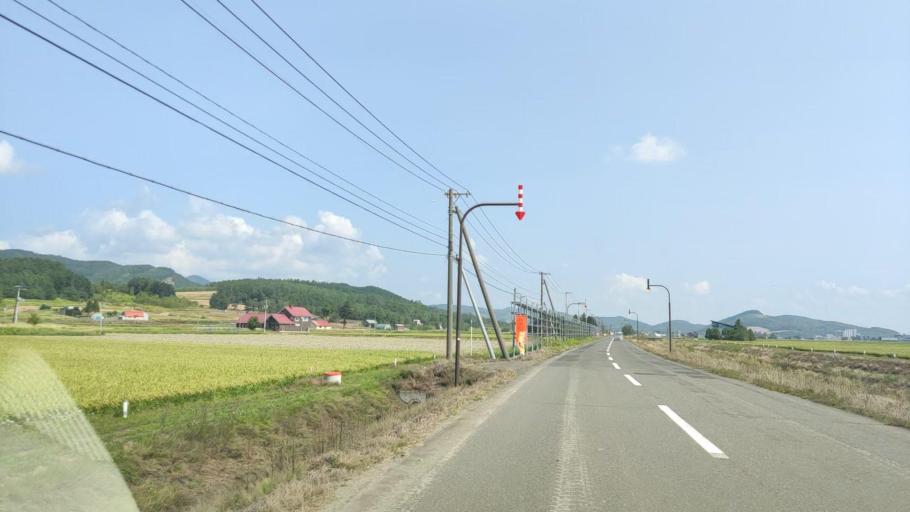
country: JP
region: Hokkaido
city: Shimo-furano
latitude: 43.3727
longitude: 142.3883
